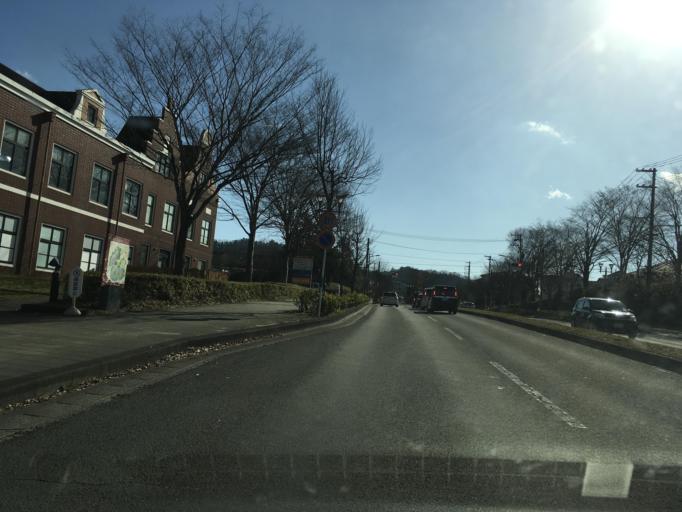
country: JP
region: Miyagi
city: Sendai
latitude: 38.2573
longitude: 140.7636
